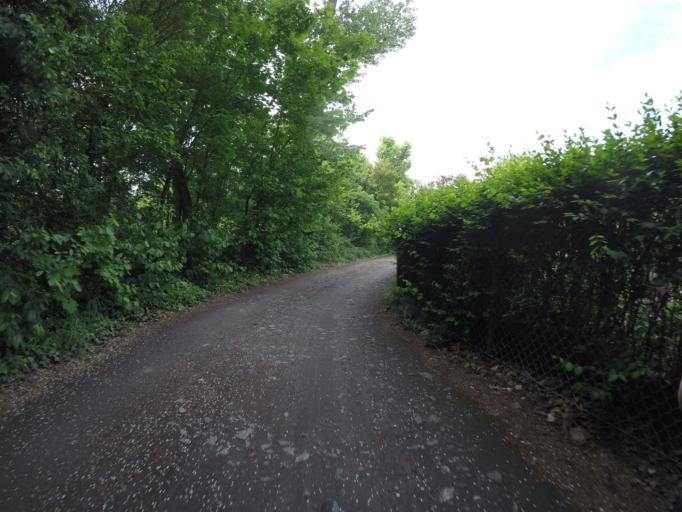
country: DE
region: Berlin
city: Reinickendorf
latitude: 52.5494
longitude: 13.3232
